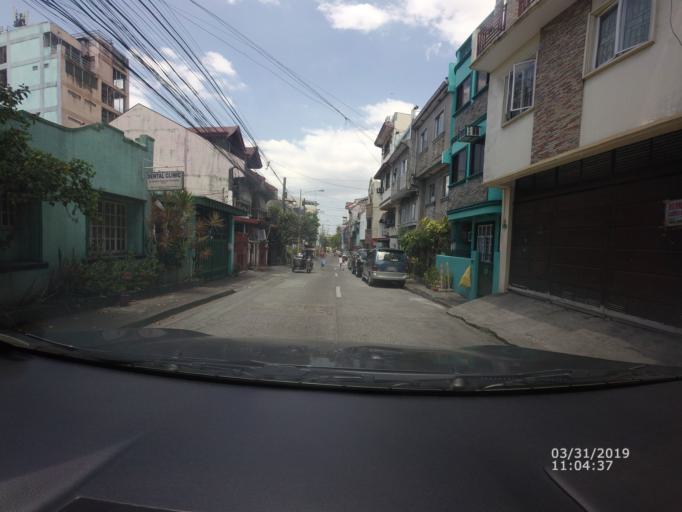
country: PH
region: Metro Manila
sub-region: Mandaluyong
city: Mandaluyong City
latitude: 14.5783
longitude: 121.0401
